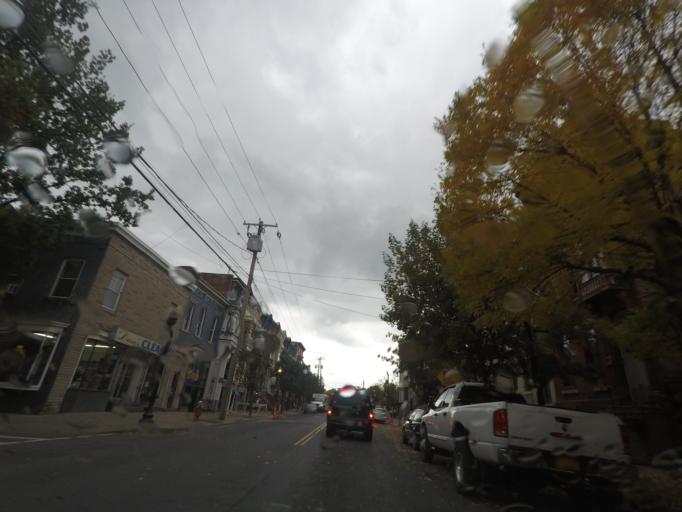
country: US
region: New York
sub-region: Albany County
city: Albany
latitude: 42.6533
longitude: -73.7669
